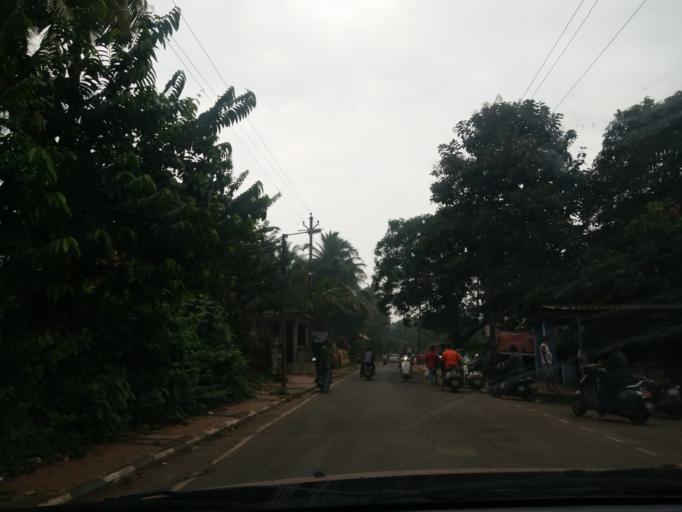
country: IN
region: Goa
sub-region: South Goa
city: Sancoale
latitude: 15.3577
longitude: 73.9273
